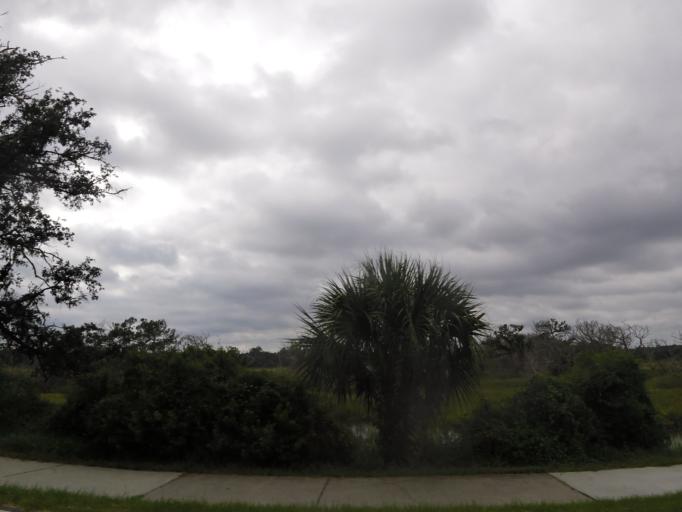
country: US
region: Georgia
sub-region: Glynn County
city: Saint Simons Island
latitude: 31.1454
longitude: -81.3754
